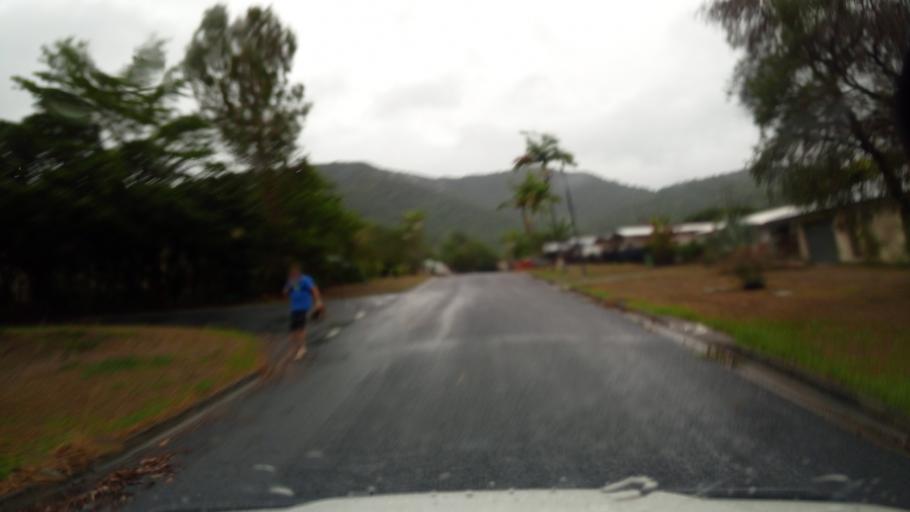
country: AU
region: Queensland
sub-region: Cairns
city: Woree
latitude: -16.9557
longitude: 145.7336
